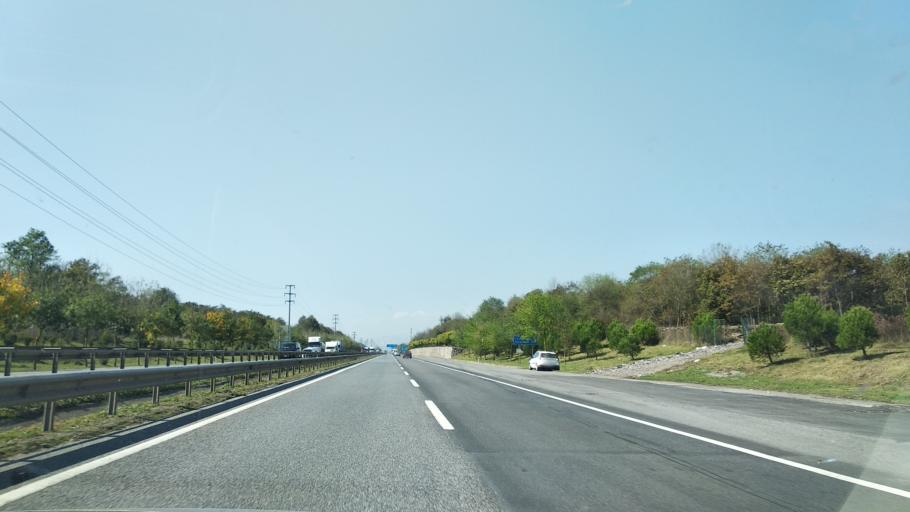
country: TR
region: Kocaeli
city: Derbent
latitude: 40.7409
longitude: 30.0922
